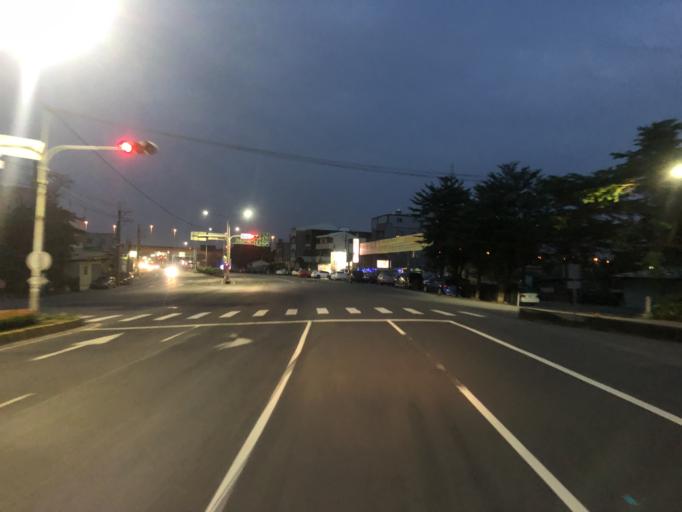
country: TW
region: Taiwan
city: Yujing
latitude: 23.1603
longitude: 120.3410
